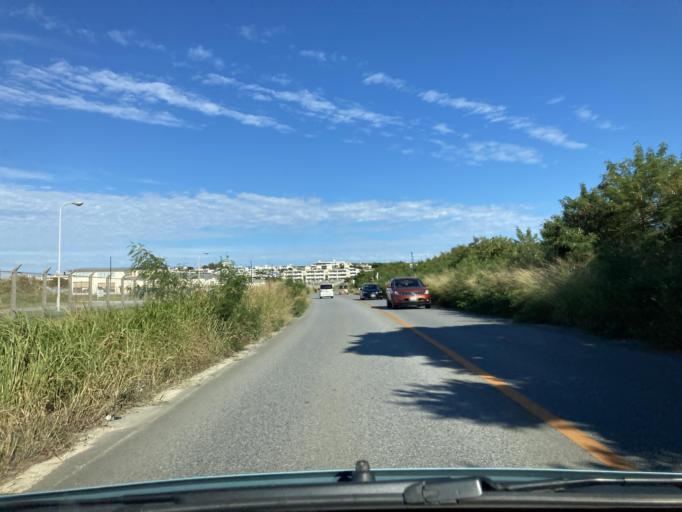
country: JP
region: Okinawa
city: Okinawa
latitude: 26.3756
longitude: 127.7458
